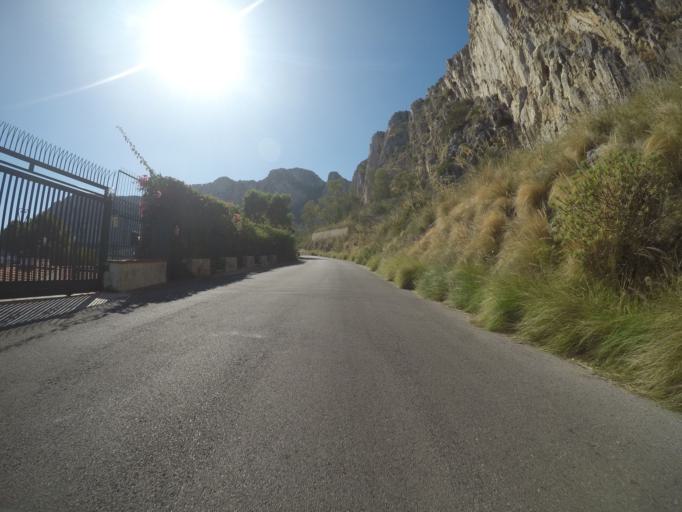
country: IT
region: Sicily
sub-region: Palermo
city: Palermo
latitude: 38.1940
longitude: 13.3388
